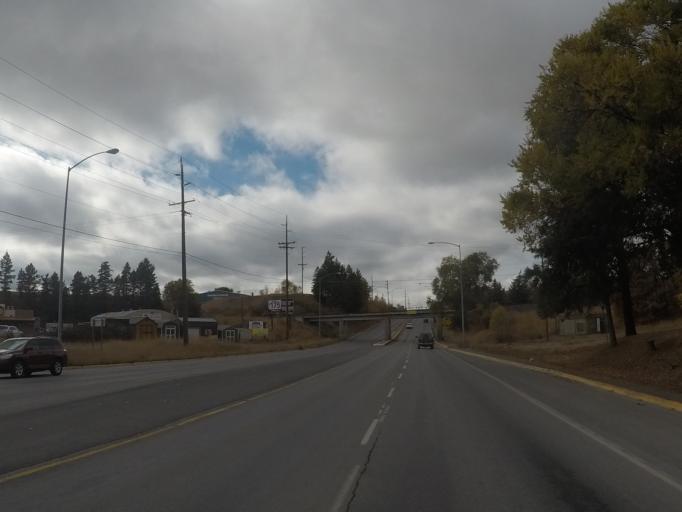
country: US
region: Montana
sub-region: Flathead County
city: Kalispell
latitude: 48.2056
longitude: -114.2962
